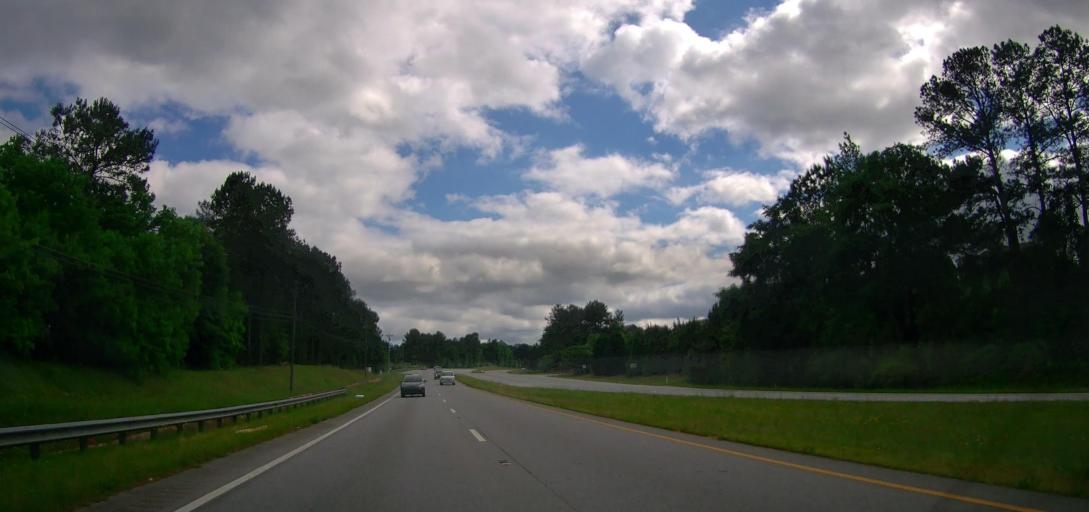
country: US
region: Georgia
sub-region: Rockdale County
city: Conyers
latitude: 33.6864
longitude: -83.9622
